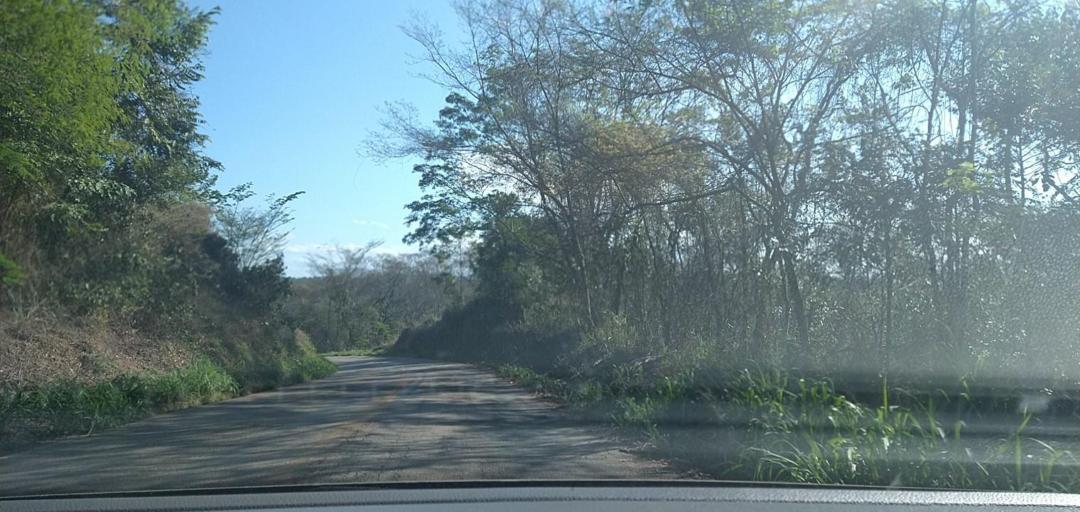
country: BR
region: Minas Gerais
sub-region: Ponte Nova
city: Ponte Nova
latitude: -20.2326
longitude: -42.9013
